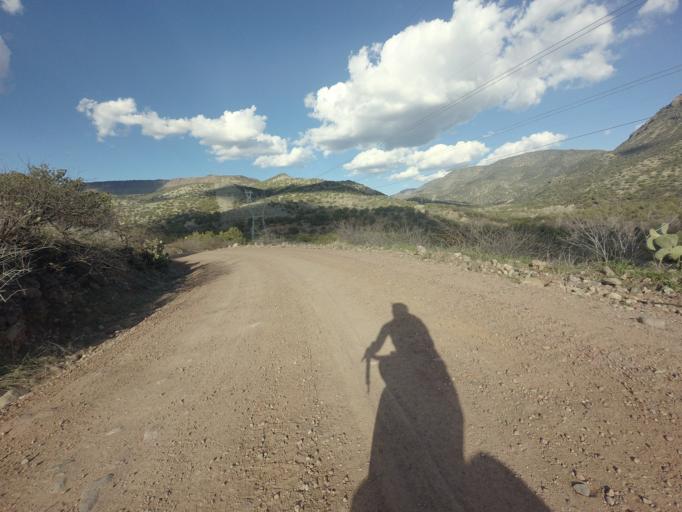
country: US
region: Arizona
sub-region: Gila County
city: Pine
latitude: 34.3928
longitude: -111.6520
